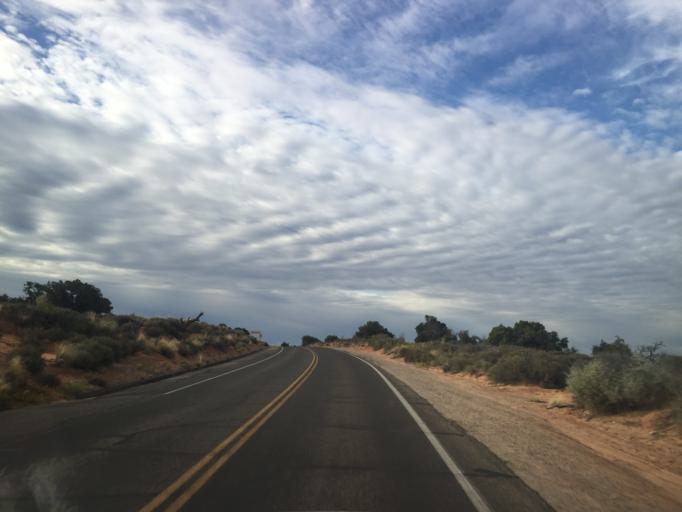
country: US
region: Utah
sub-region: Grand County
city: Moab
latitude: 38.7643
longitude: -109.5838
